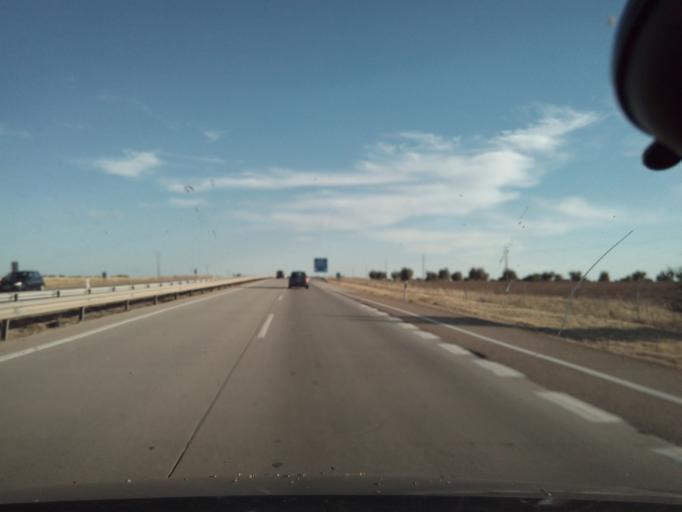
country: ES
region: Castille-La Mancha
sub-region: Province of Toledo
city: Dosbarrios
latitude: 39.8455
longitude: -3.4730
